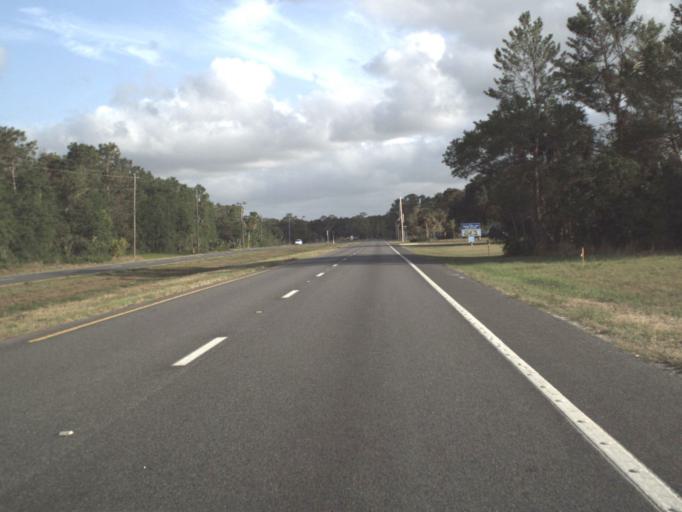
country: US
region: Florida
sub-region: Brevard County
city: Mims
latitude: 28.7256
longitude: -80.8644
